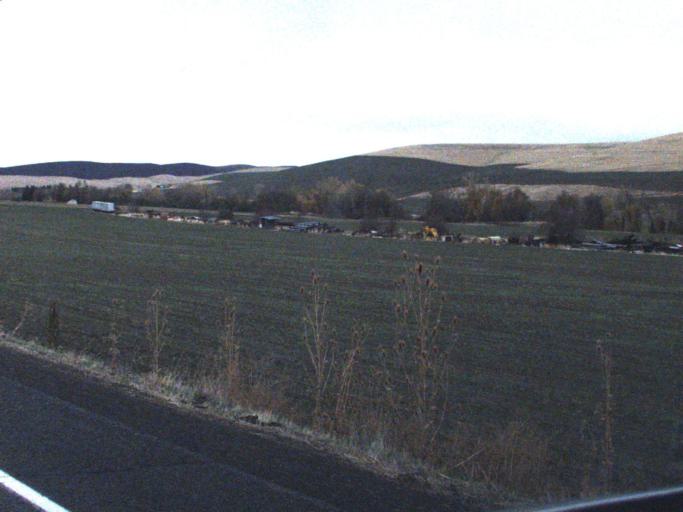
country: US
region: Washington
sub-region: Walla Walla County
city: Waitsburg
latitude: 46.2393
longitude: -118.1428
